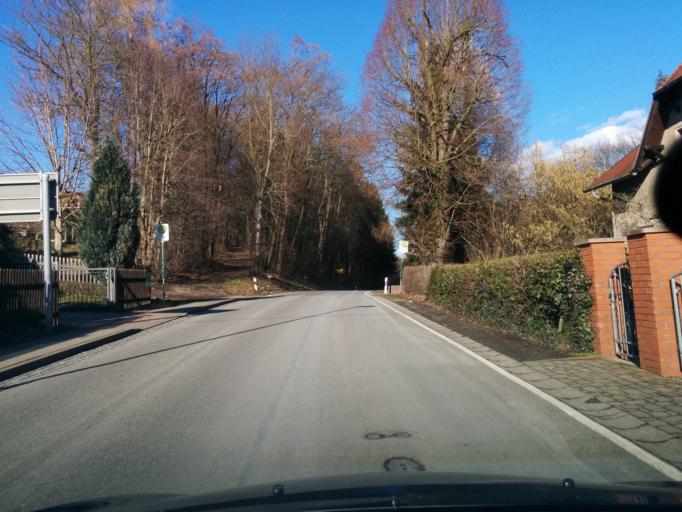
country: DE
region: Saxony
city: Augustusburg
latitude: 50.8218
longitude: 13.0786
